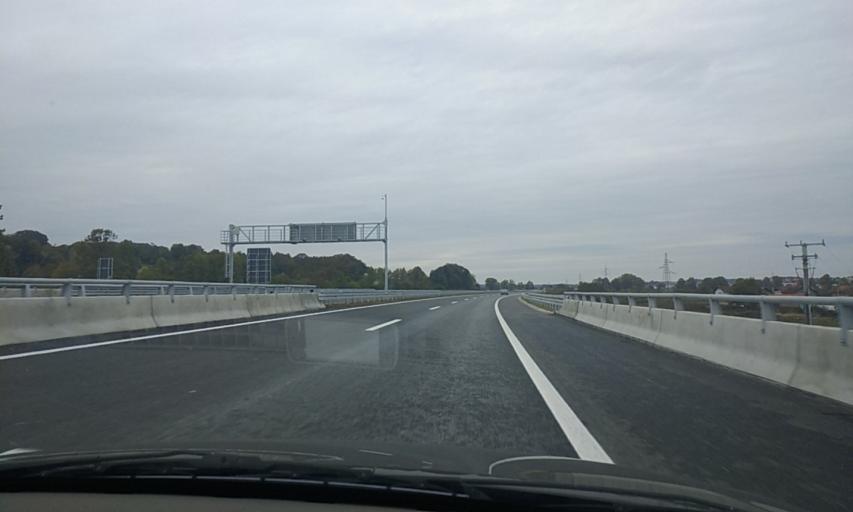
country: BA
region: Republika Srpska
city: Prnjavor
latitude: 44.8525
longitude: 17.6647
